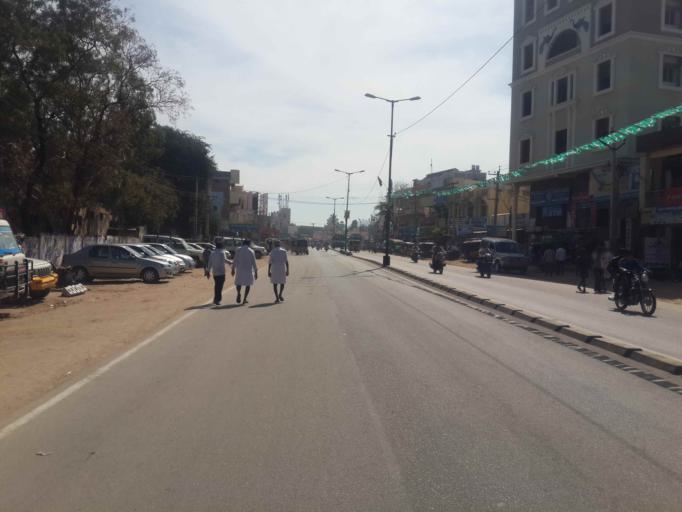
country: IN
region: Andhra Pradesh
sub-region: Anantapur
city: Kadiri
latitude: 14.1161
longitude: 78.1589
